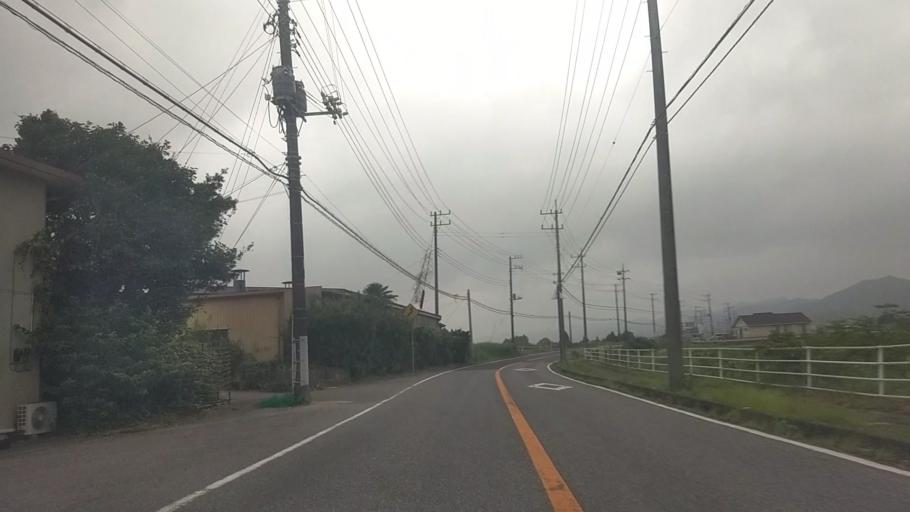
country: JP
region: Chiba
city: Kawaguchi
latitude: 35.1234
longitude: 140.0618
